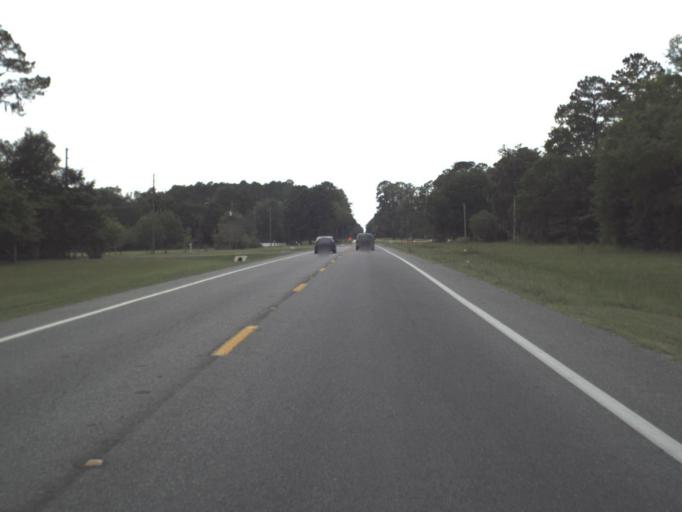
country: US
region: Florida
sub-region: Hamilton County
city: Jasper
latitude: 30.5244
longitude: -82.9715
